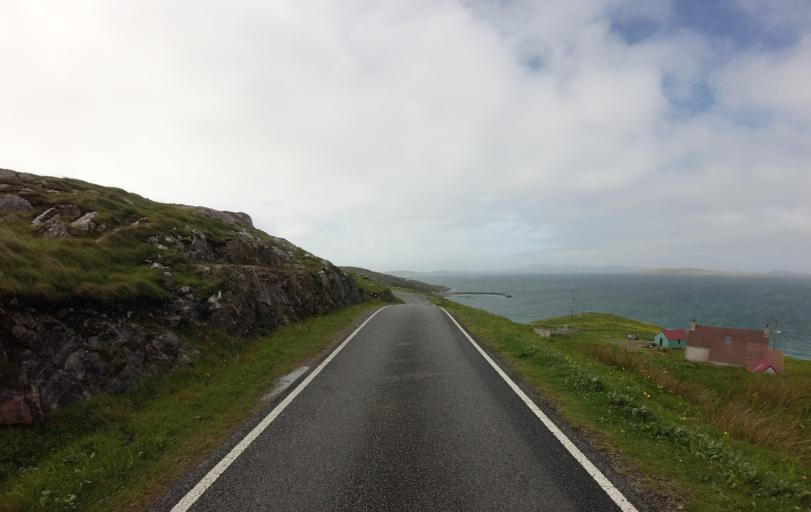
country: GB
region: Scotland
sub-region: Eilean Siar
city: Isle of South Uist
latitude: 57.0767
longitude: -7.3028
